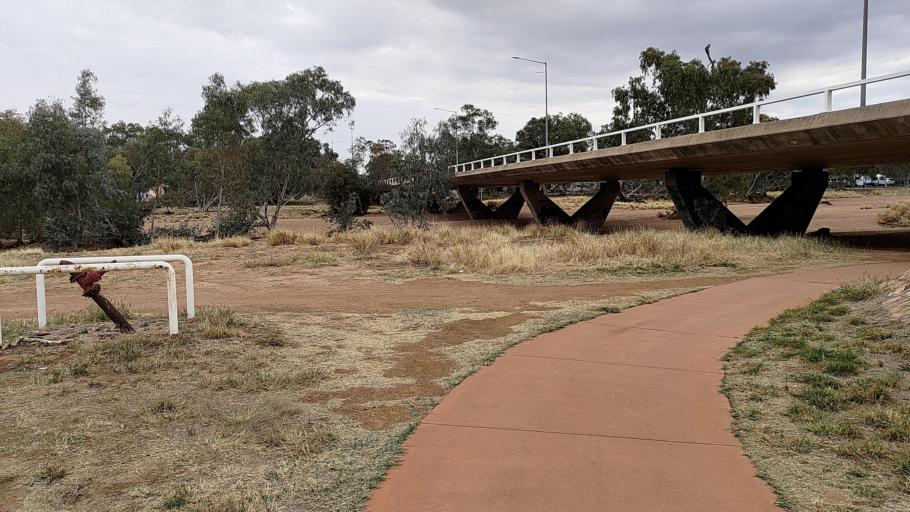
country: AU
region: Northern Territory
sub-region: Alice Springs
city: Alice Springs
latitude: -23.7033
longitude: 133.8848
